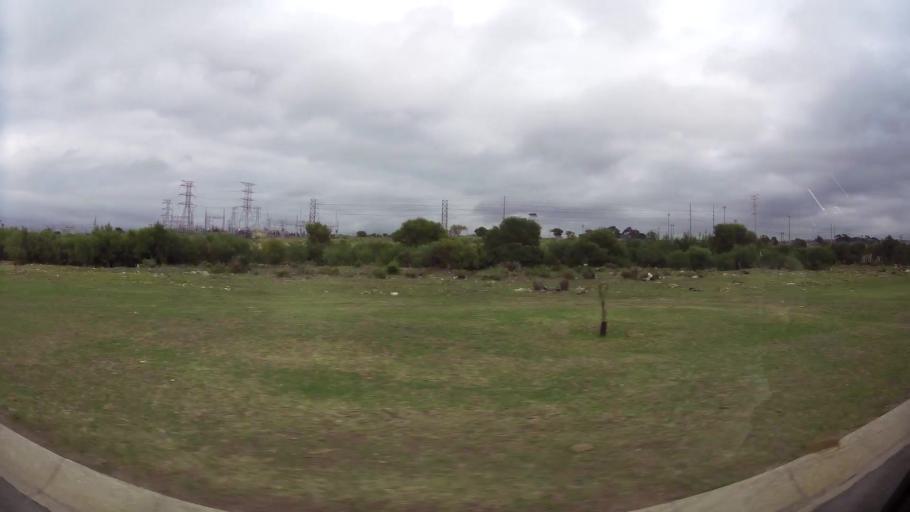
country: ZA
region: Eastern Cape
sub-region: Nelson Mandela Bay Metropolitan Municipality
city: Port Elizabeth
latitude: -33.9093
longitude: 25.5669
